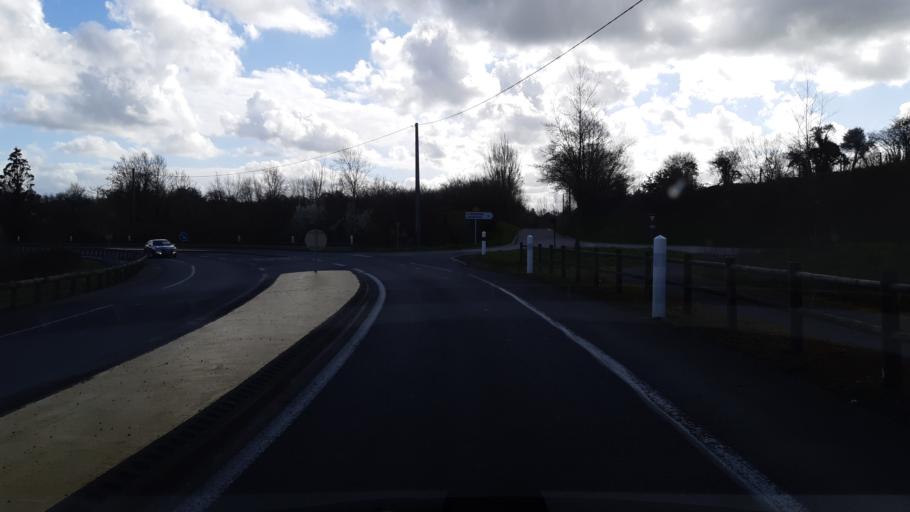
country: FR
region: Lower Normandy
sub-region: Departement de la Manche
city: Agneaux
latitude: 49.0714
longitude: -1.1302
